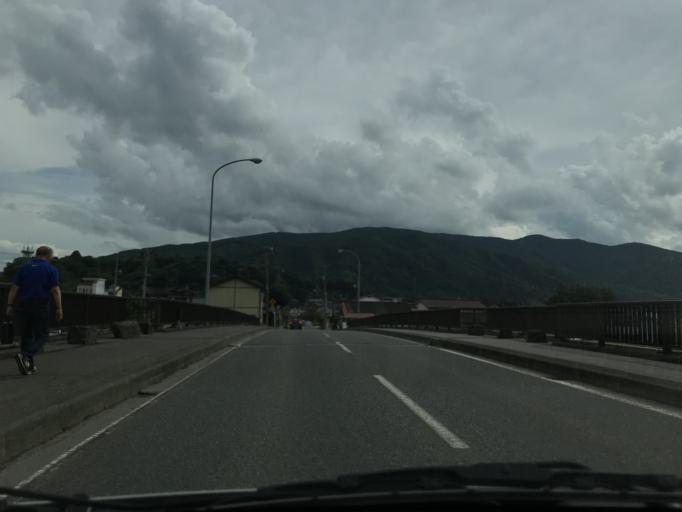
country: JP
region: Iwate
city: Tono
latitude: 39.3345
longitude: 141.5290
